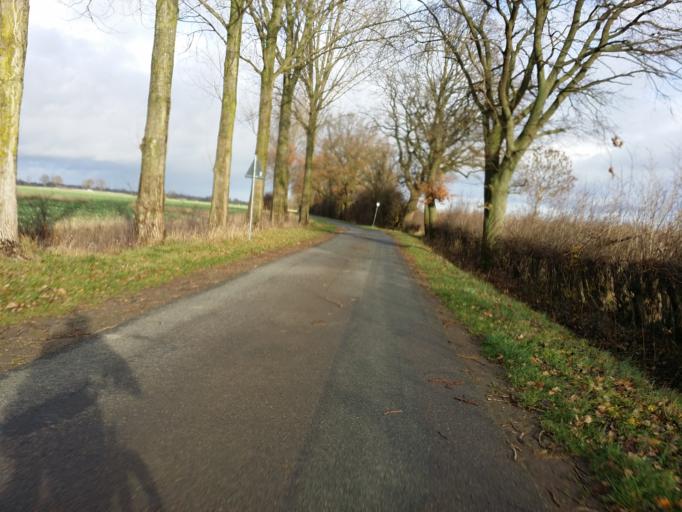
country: DE
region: Lower Saxony
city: Riede
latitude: 52.9827
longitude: 8.9752
